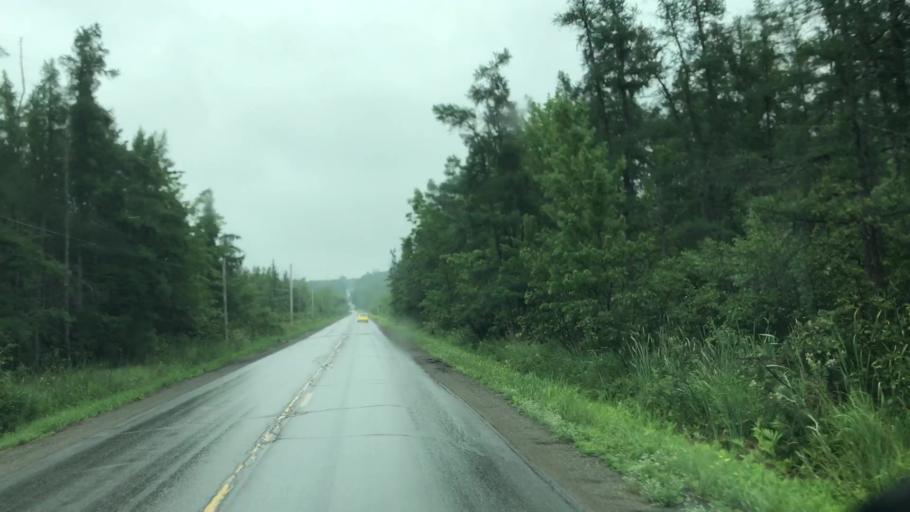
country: US
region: Maine
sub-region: Penobscot County
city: Veazie
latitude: 44.8680
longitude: -68.7163
